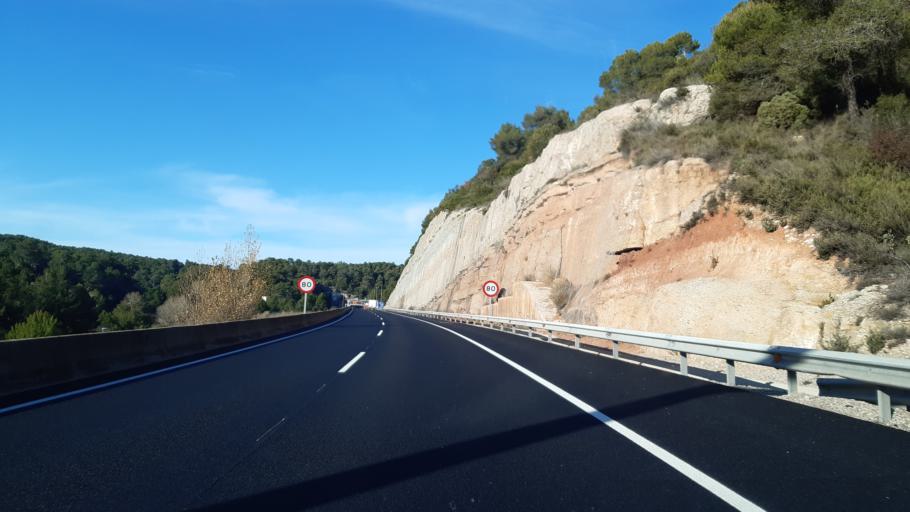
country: ES
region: Catalonia
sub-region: Provincia de Barcelona
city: Castelloli
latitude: 41.5955
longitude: 1.7463
